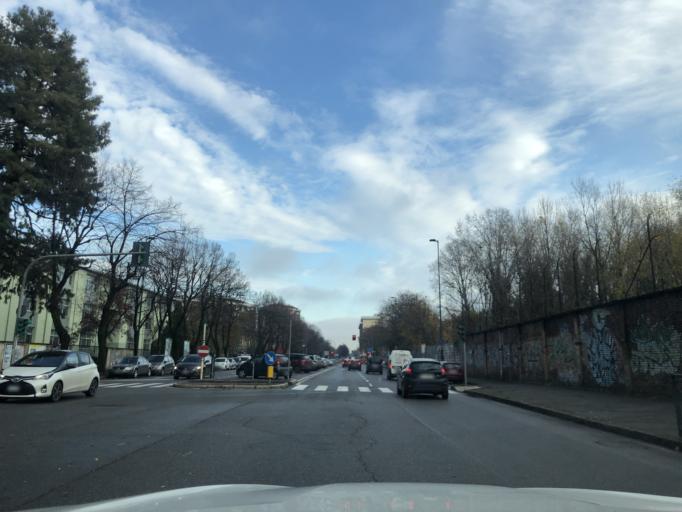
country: IT
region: Lombardy
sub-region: Citta metropolitana di Milano
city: Sesto San Giovanni
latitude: 45.5340
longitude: 9.2426
